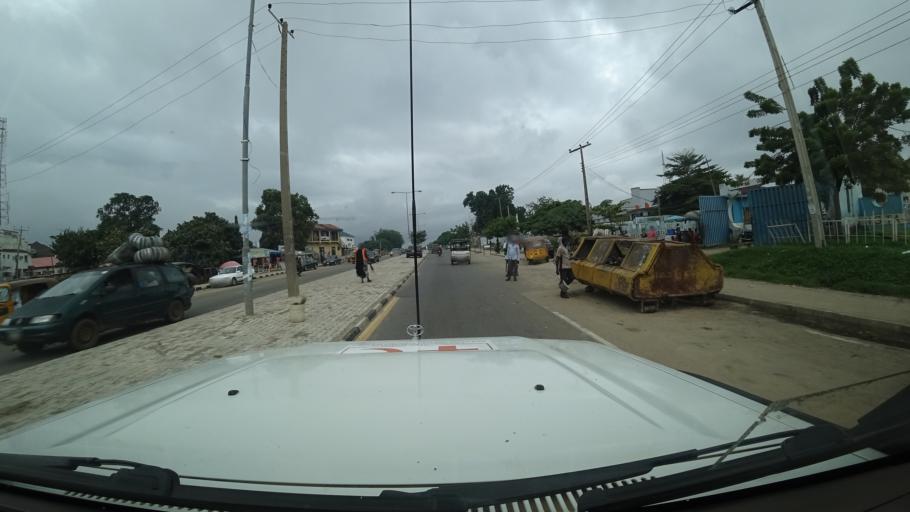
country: NG
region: Niger
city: Minna
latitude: 9.6026
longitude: 6.5580
